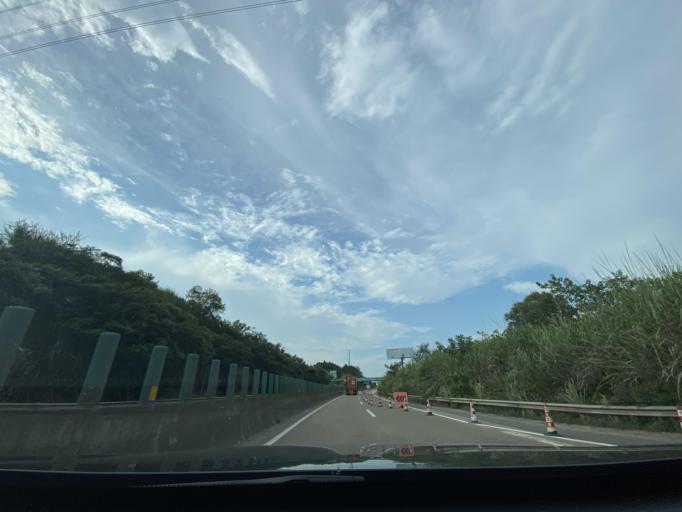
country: CN
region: Sichuan
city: Yanjiang
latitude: 30.0582
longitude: 104.5969
